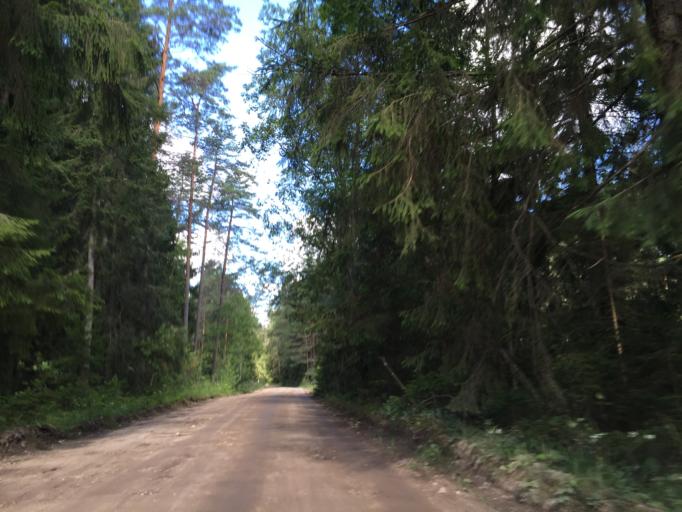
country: LV
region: Garkalne
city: Garkalne
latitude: 56.9725
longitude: 24.4628
